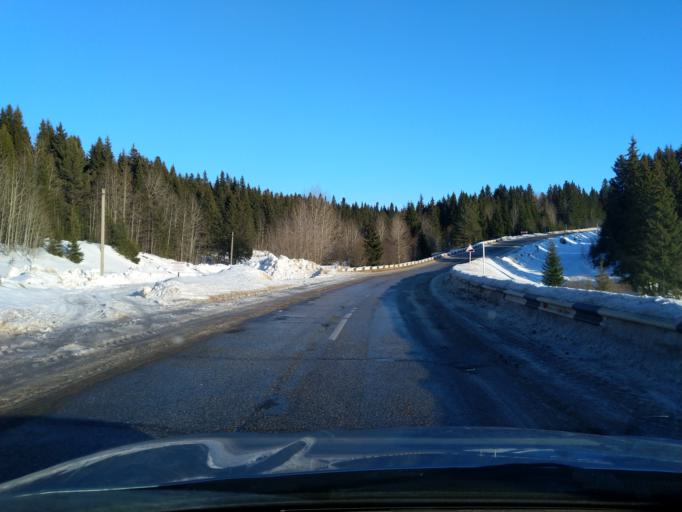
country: RU
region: Perm
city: Polazna
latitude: 58.3097
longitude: 56.4666
